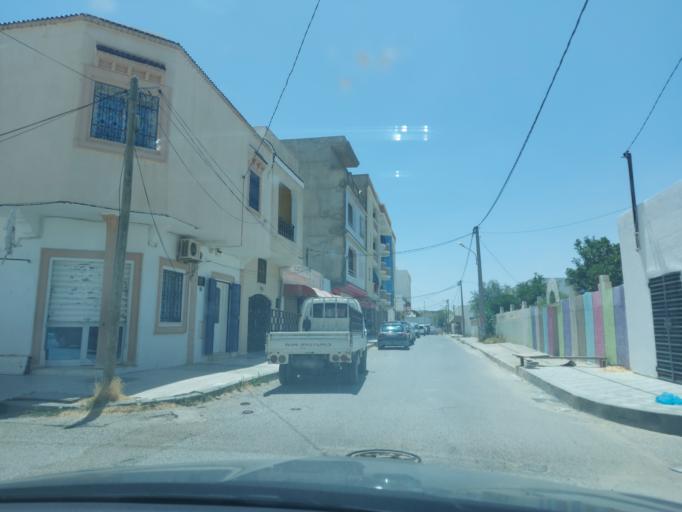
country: TN
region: Silyanah
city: Siliana
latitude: 36.0859
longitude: 9.3681
